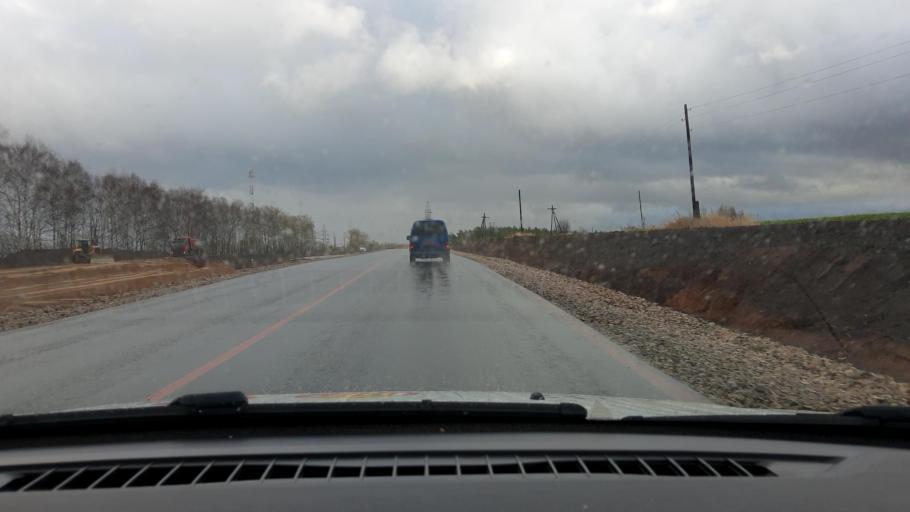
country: RU
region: Nizjnij Novgorod
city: Pamyat' Parizhskoy Kommuny
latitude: 56.0273
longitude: 44.5710
